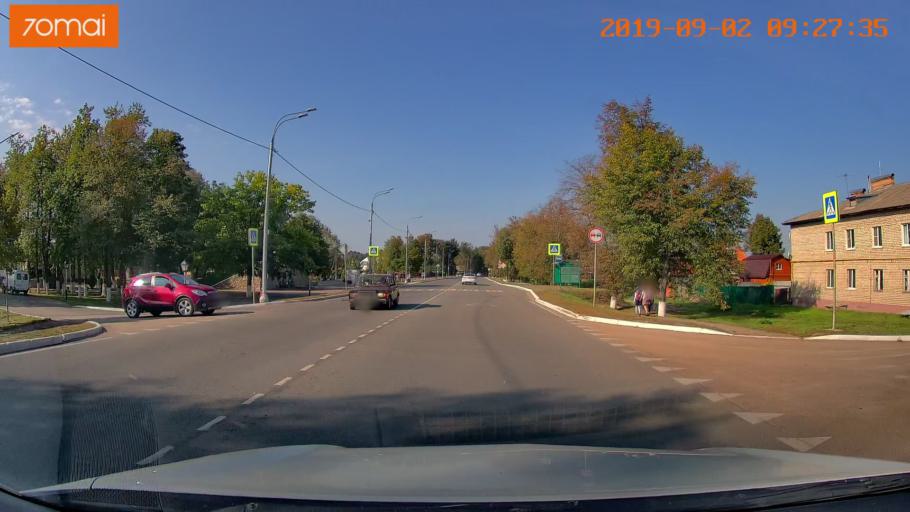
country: RU
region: Kaluga
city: Yukhnov
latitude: 54.7450
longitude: 35.2412
